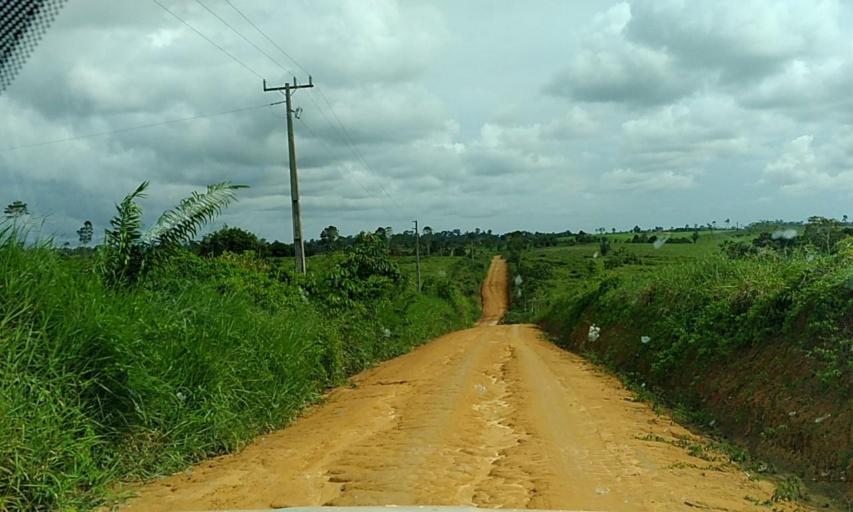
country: BR
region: Para
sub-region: Altamira
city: Altamira
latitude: -3.2591
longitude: -52.6944
